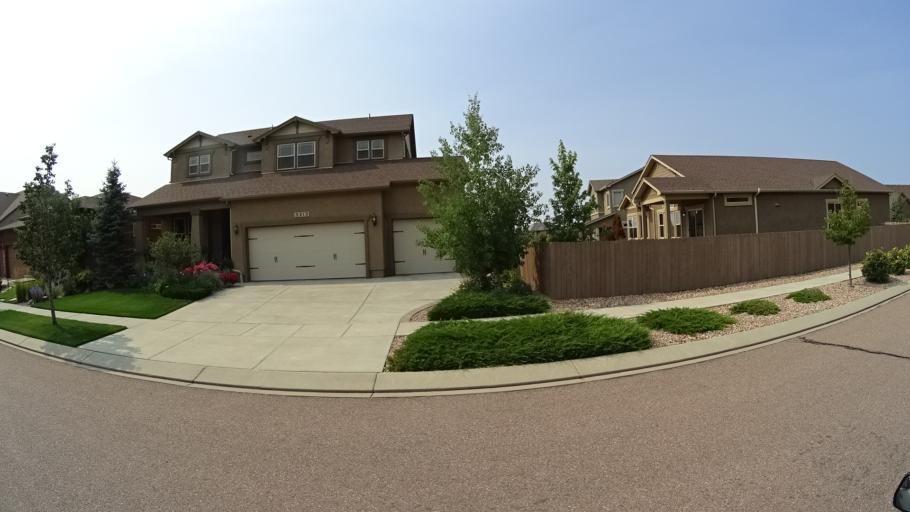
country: US
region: Colorado
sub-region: El Paso County
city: Black Forest
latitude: 38.9696
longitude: -104.7308
